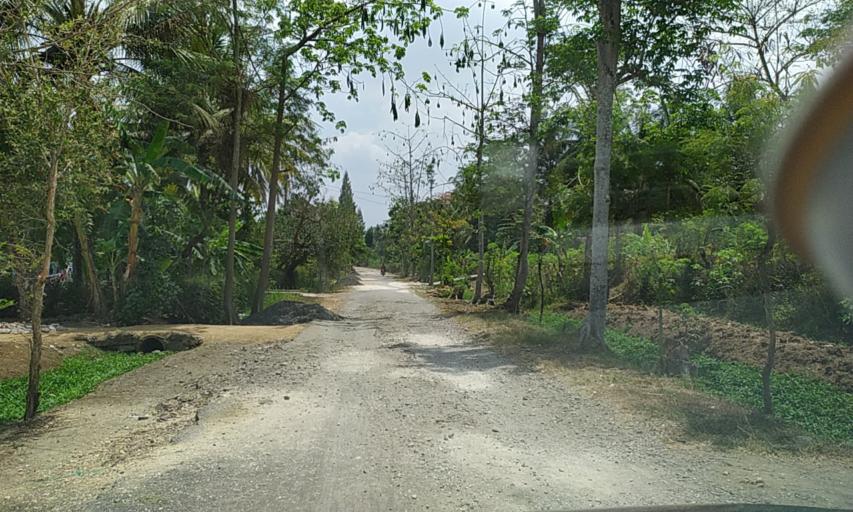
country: ID
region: Central Java
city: Cipariuk
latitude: -7.4998
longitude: 108.7660
